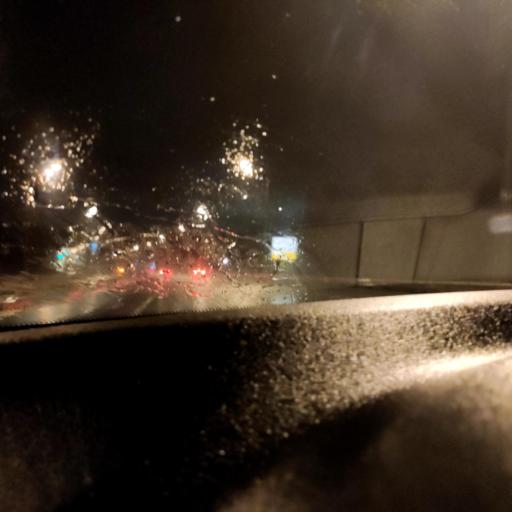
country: RU
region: Samara
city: Petra-Dubrava
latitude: 53.3125
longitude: 50.2314
